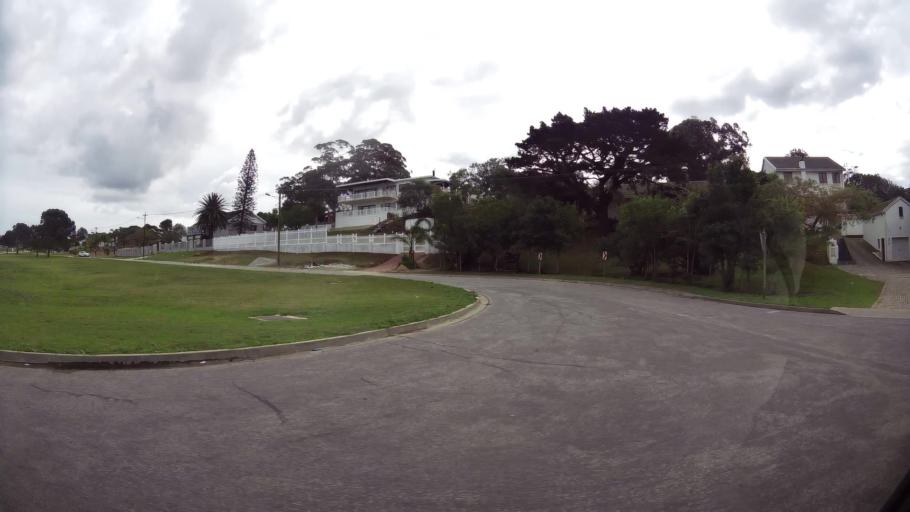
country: ZA
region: Eastern Cape
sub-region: Nelson Mandela Bay Metropolitan Municipality
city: Port Elizabeth
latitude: -33.9365
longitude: 25.5181
